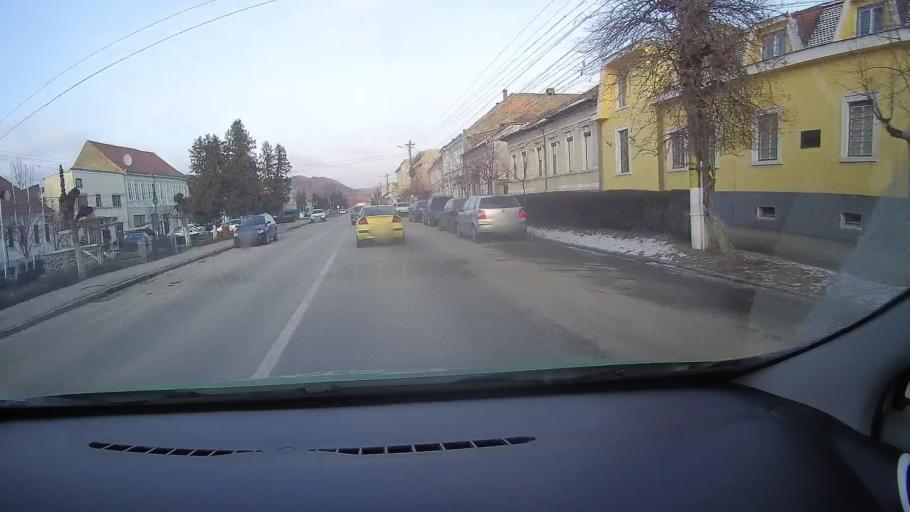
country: RO
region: Harghita
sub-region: Oras Cristuru Secuiesc
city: Cristuru Secuiesc
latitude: 46.2897
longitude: 25.0331
